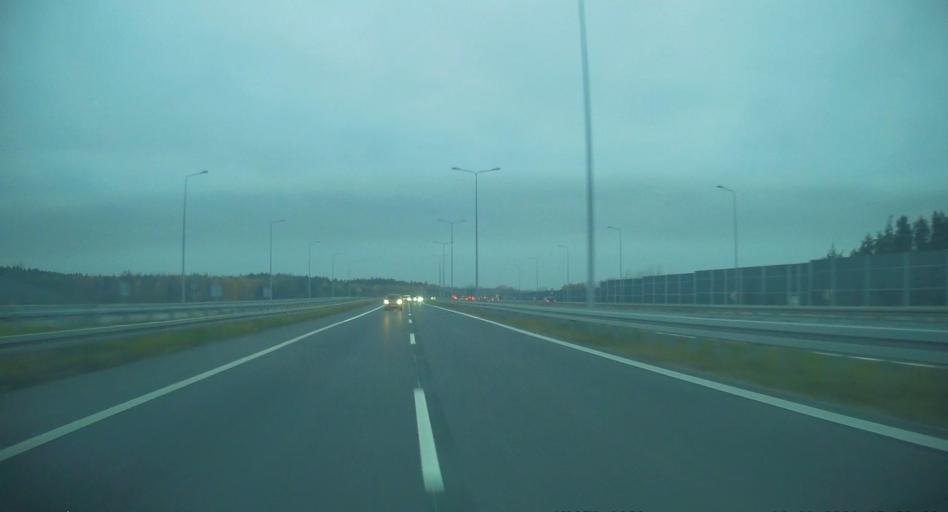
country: PL
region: Silesian Voivodeship
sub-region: Powiat tarnogorski
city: Ozarowice
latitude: 50.4524
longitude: 19.0781
